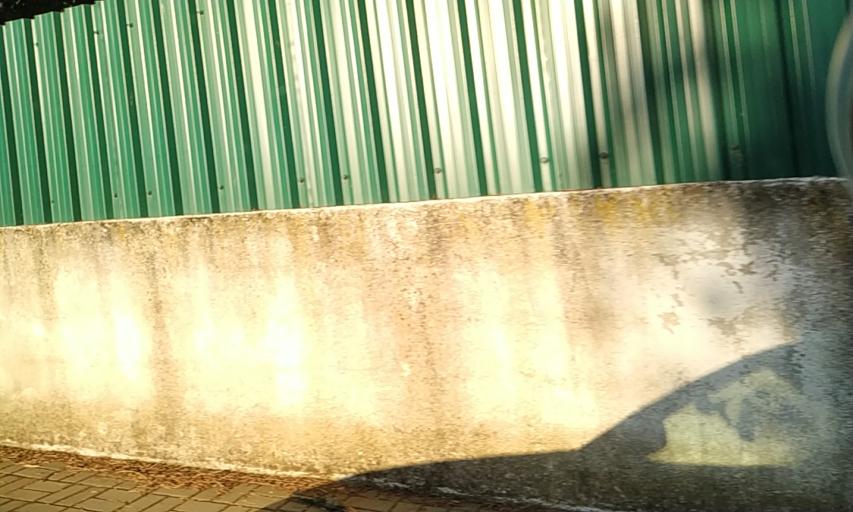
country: PT
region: Portalegre
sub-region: Marvao
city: Marvao
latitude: 39.3736
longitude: -7.3886
